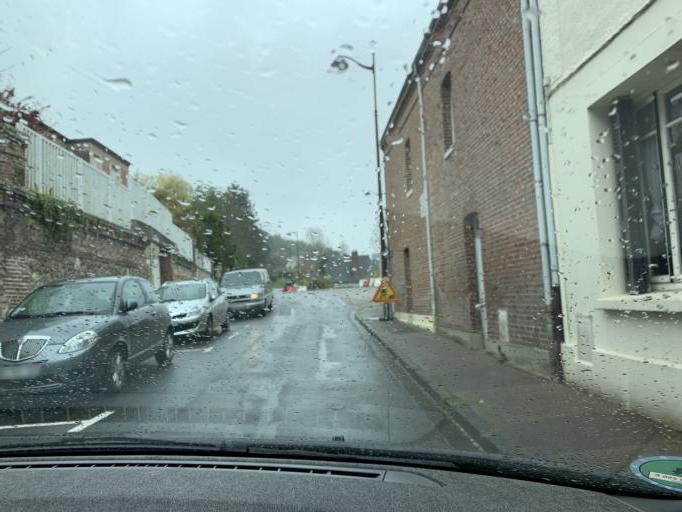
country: FR
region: Haute-Normandie
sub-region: Departement de la Seine-Maritime
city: Etretat
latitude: 49.7088
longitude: 0.2137
